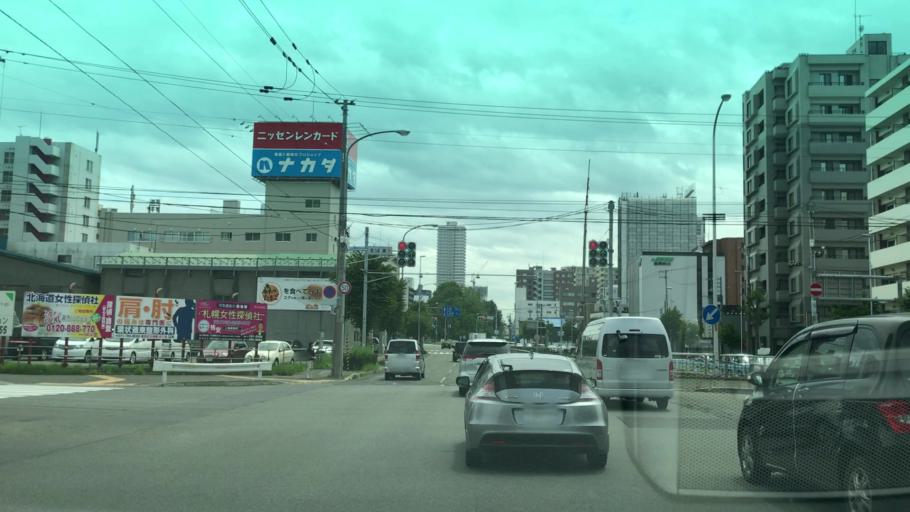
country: JP
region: Hokkaido
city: Sapporo
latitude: 43.0789
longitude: 141.3521
